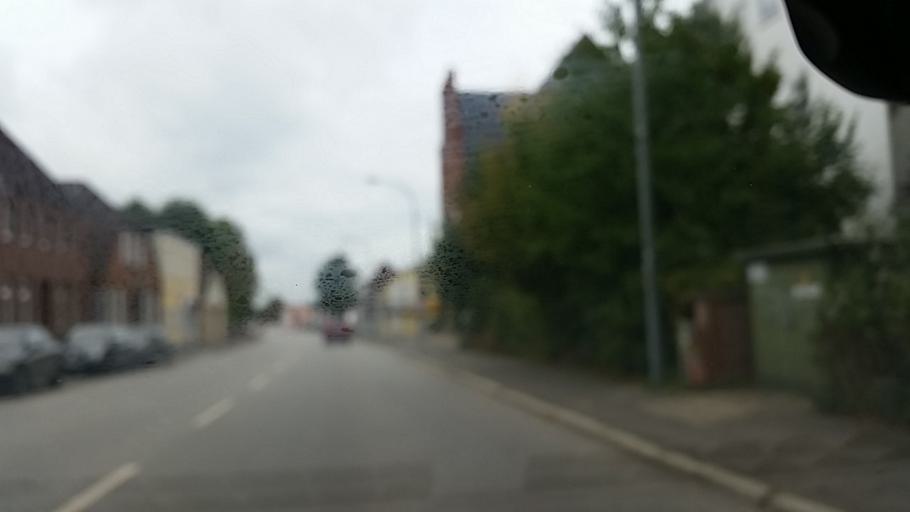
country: DE
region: Schleswig-Holstein
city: Bad Segeberg
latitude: 53.9370
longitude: 10.3023
